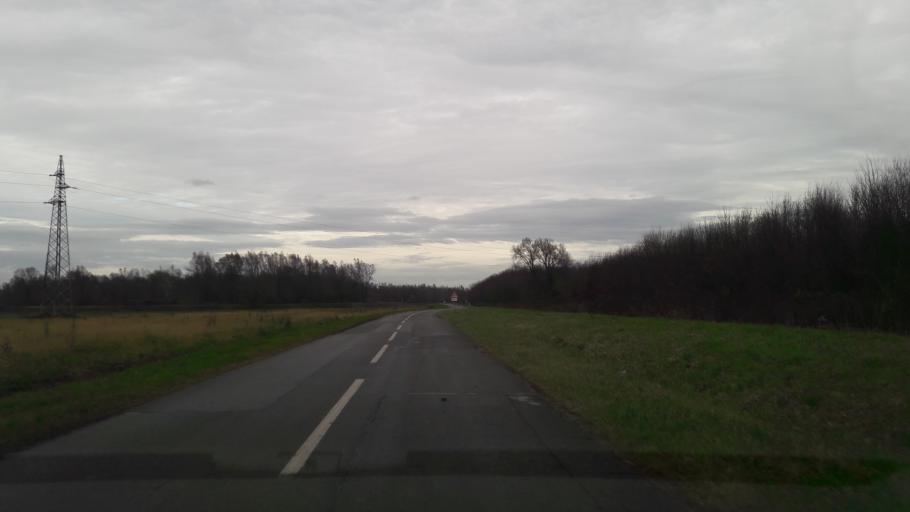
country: HR
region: Osjecko-Baranjska
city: Velimirovac
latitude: 45.6174
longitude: 18.0734
